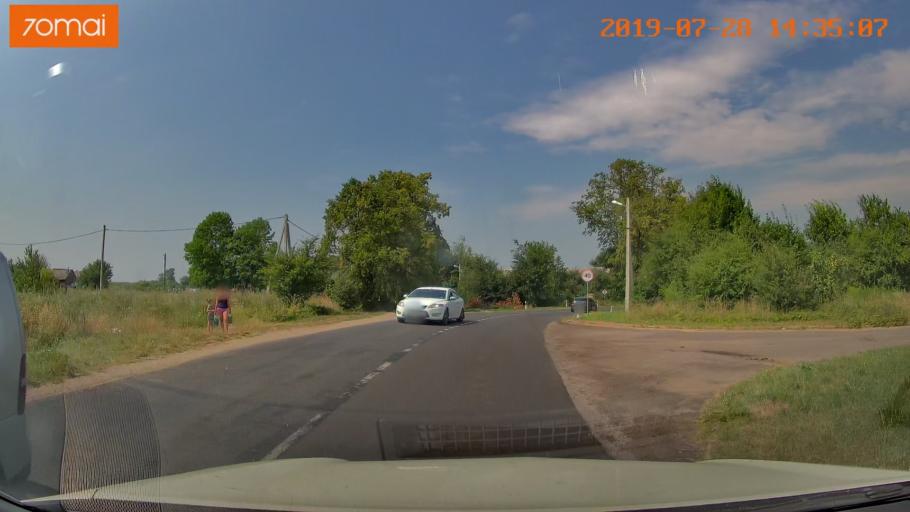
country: RU
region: Kaliningrad
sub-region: Gorod Kaliningrad
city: Yantarnyy
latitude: 54.8291
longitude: 20.0111
